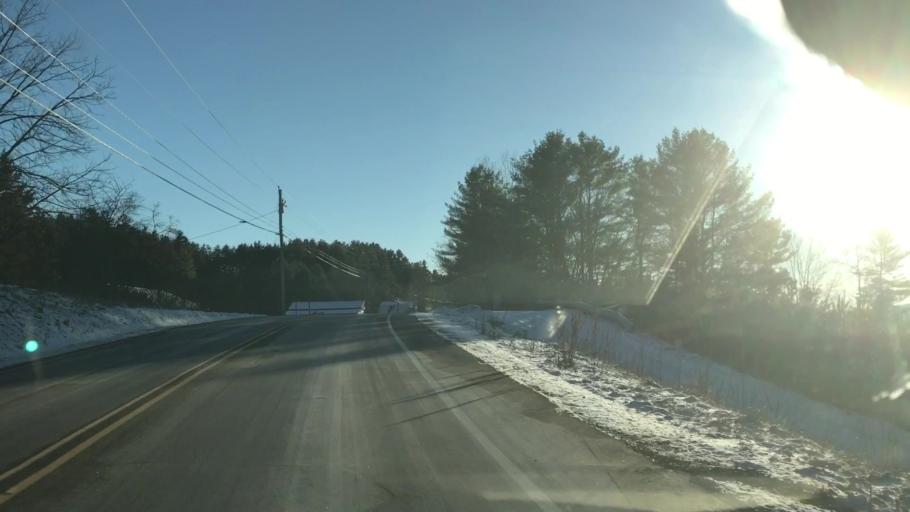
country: US
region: New Hampshire
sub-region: Grafton County
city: Orford
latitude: 43.9228
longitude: -72.1135
